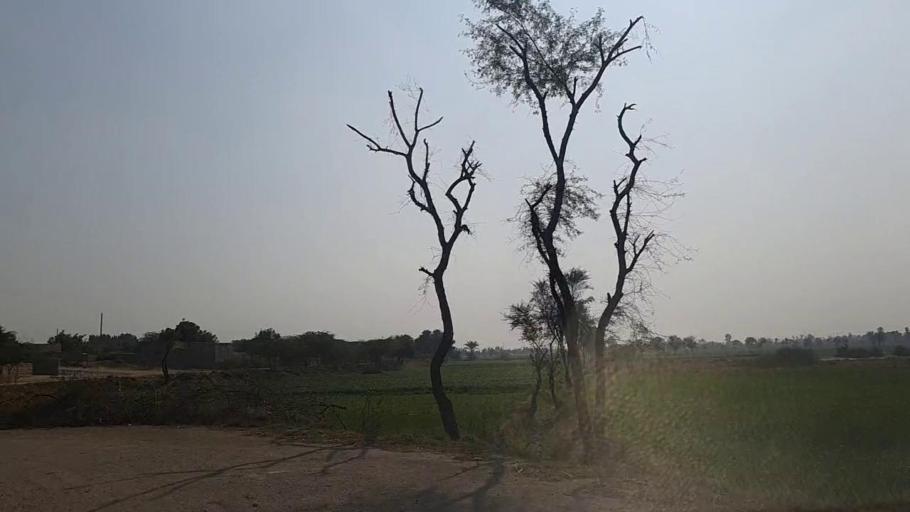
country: PK
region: Sindh
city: Daur
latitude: 26.4666
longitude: 68.4560
